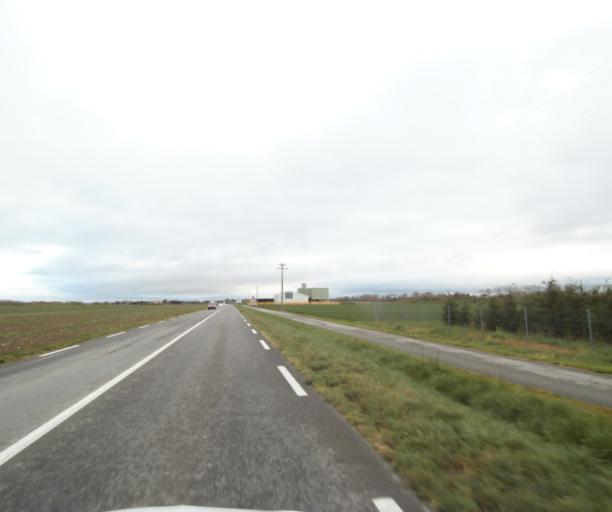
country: FR
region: Midi-Pyrenees
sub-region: Departement de l'Ariege
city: Saverdun
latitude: 43.1998
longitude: 1.6096
